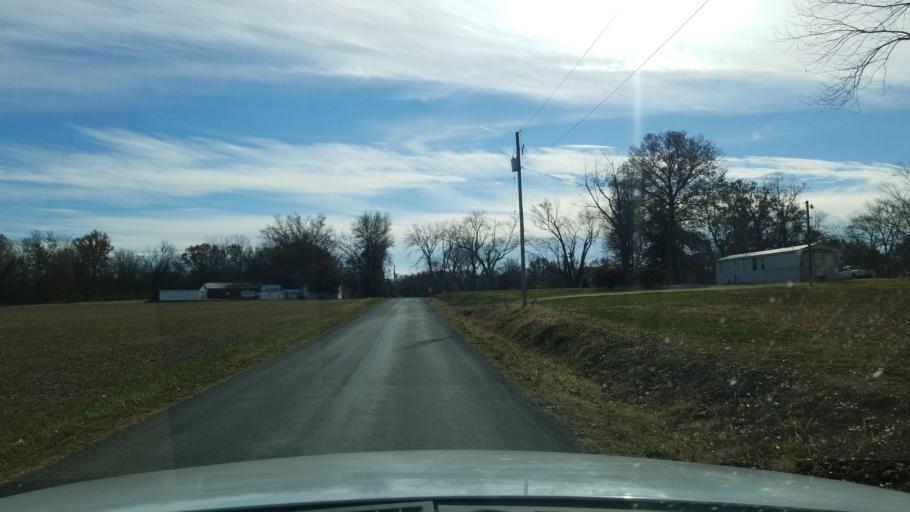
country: US
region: Illinois
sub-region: Saline County
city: Harrisburg
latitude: 37.7689
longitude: -88.5171
